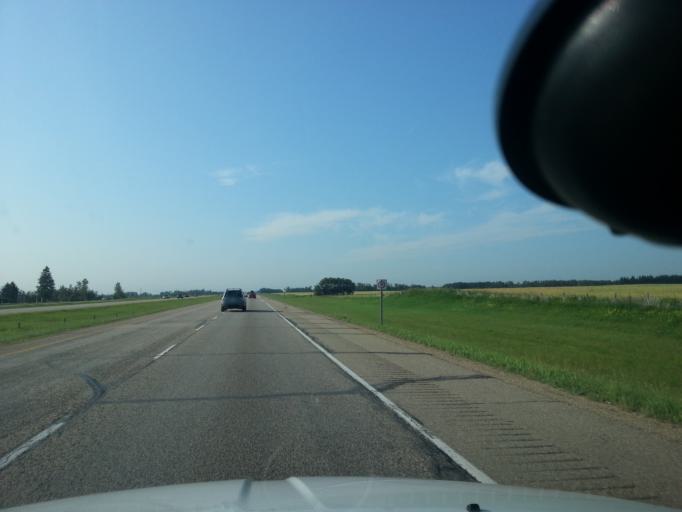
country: CA
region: Alberta
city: Ponoka
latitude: 52.8973
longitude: -113.6442
